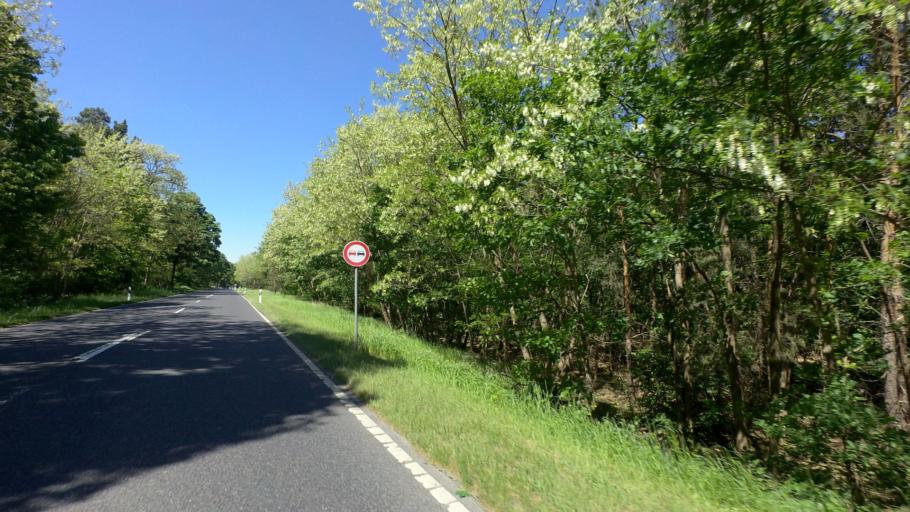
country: DE
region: Brandenburg
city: Lieberose
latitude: 51.9638
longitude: 14.3184
